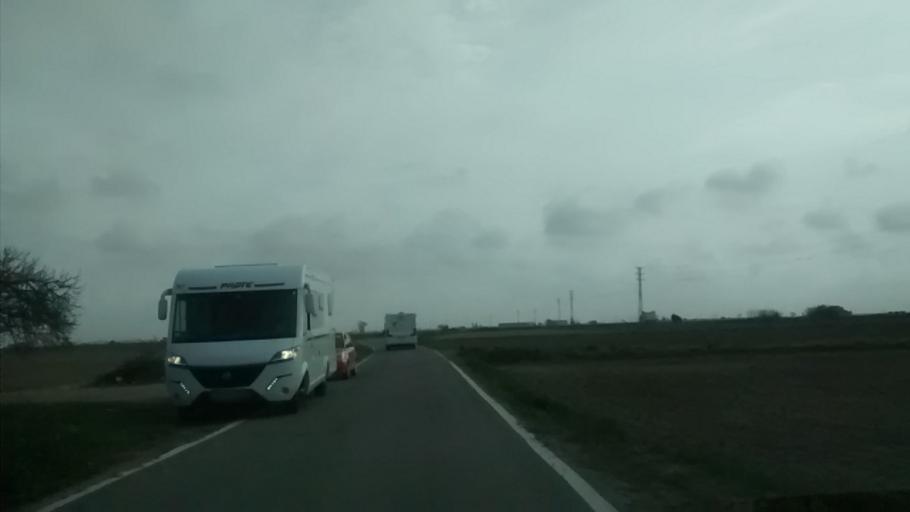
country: ES
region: Catalonia
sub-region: Provincia de Tarragona
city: Sant Carles de la Rapita
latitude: 40.6655
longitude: 0.6465
